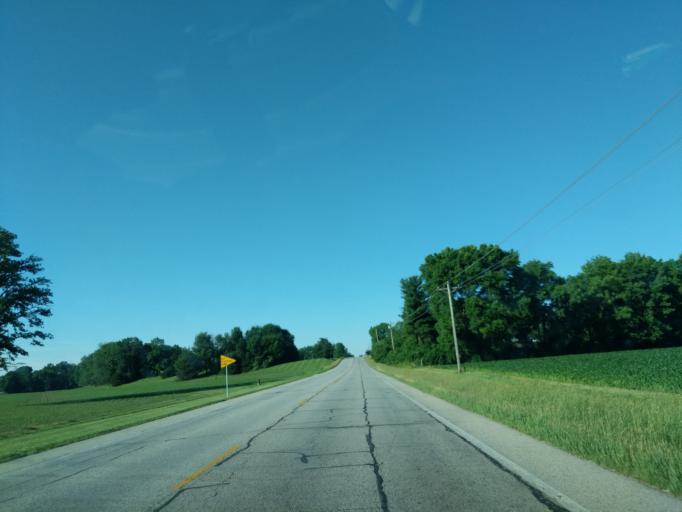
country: US
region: Indiana
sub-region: Shelby County
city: Shelbyville
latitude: 39.6071
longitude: -85.7699
